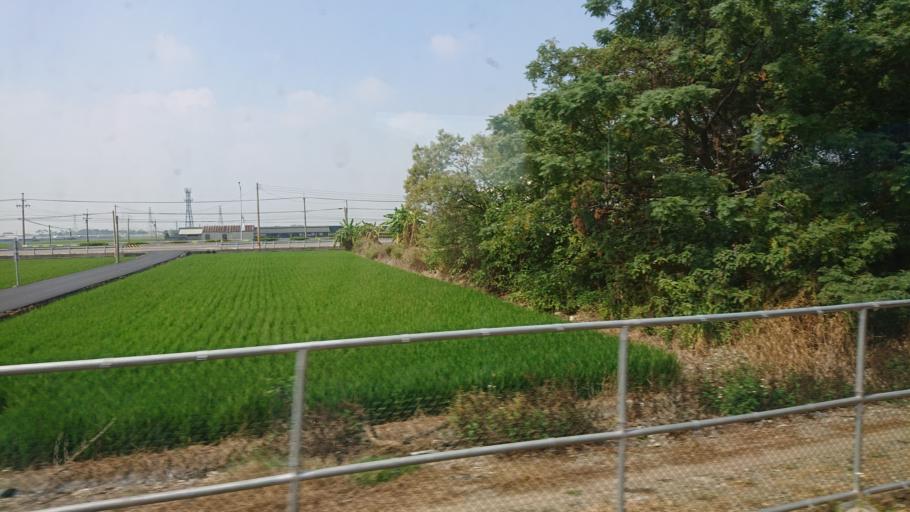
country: TW
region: Taiwan
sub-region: Yunlin
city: Douliu
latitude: 23.6481
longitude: 120.4724
